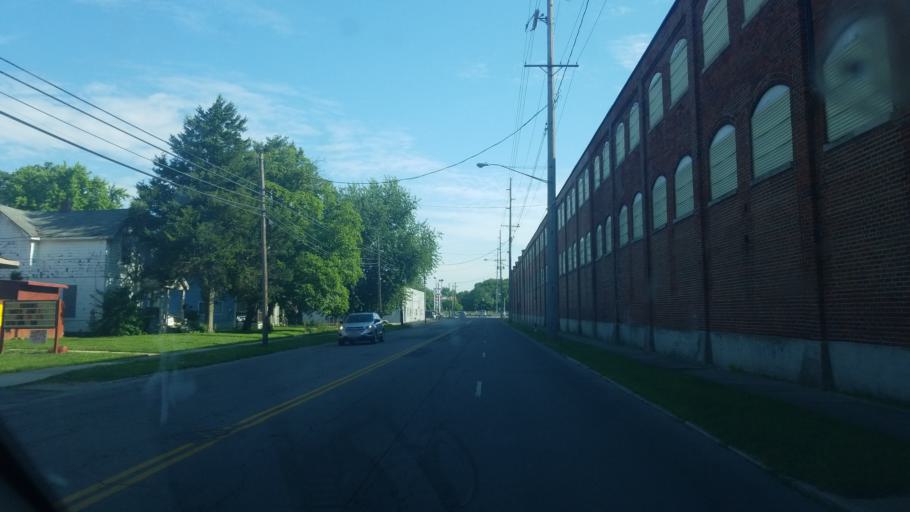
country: US
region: Ohio
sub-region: Marion County
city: Marion
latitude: 40.5864
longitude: -83.1433
